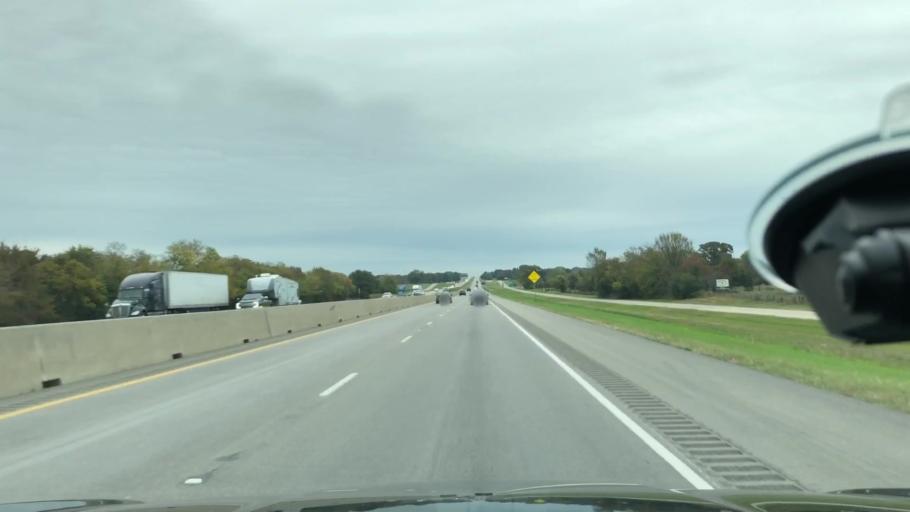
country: US
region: Texas
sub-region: Franklin County
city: Mount Vernon
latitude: 33.1658
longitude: -95.3026
